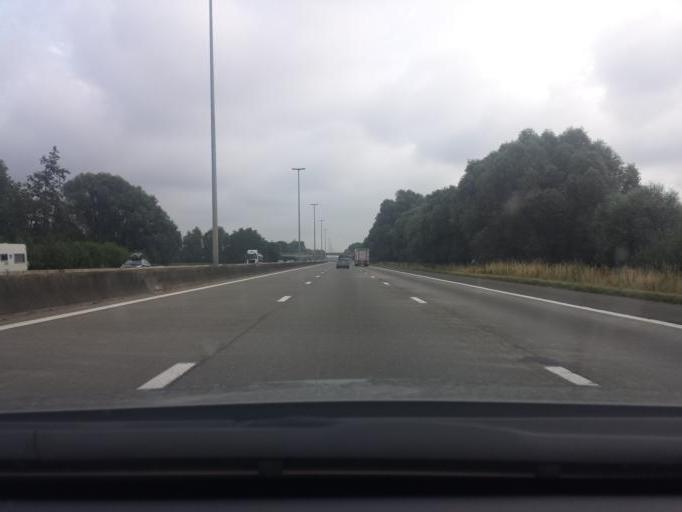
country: BE
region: Flanders
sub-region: Provincie Oost-Vlaanderen
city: Zulte
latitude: 50.8884
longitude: 3.4680
